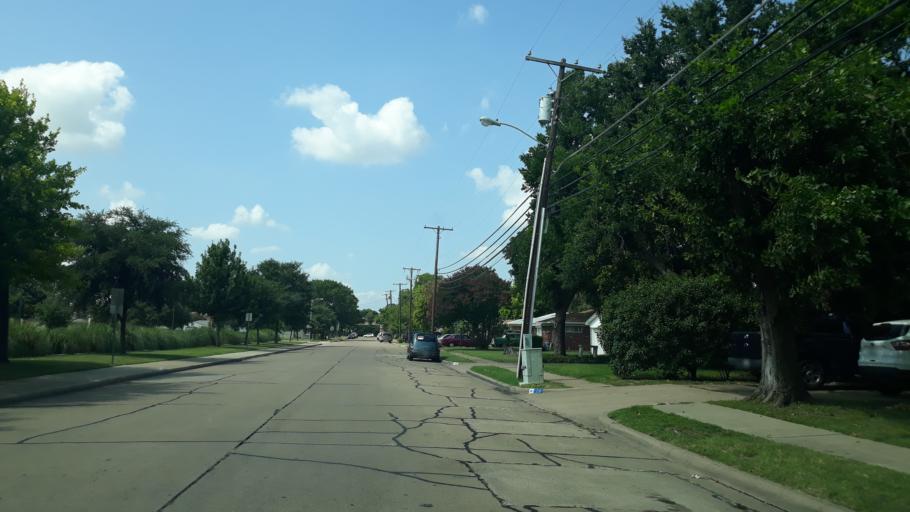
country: US
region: Texas
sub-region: Dallas County
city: Irving
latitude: 32.8124
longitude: -96.9817
